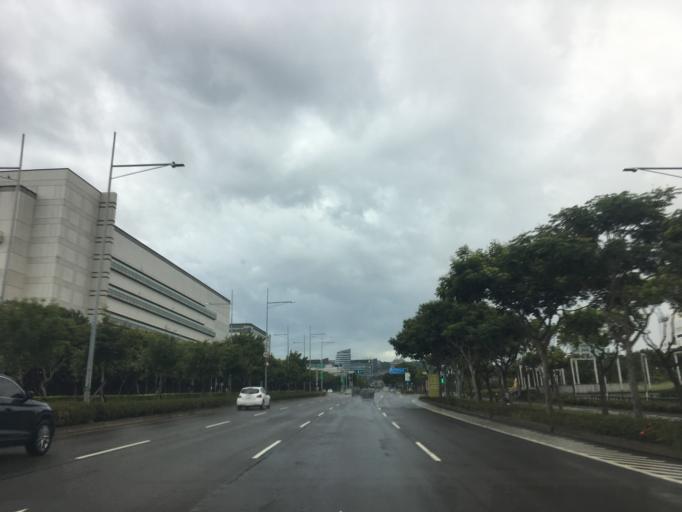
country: TW
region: Taiwan
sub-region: Taichung City
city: Taichung
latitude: 24.2070
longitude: 120.6241
